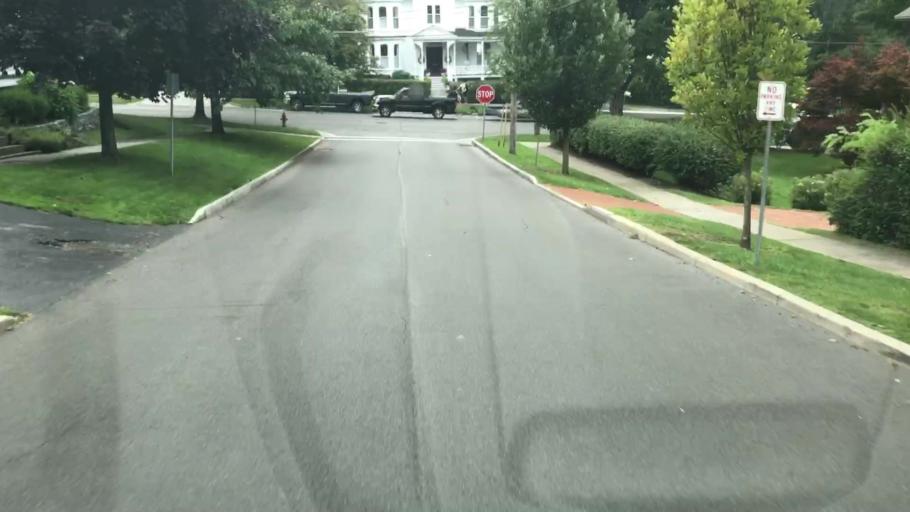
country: US
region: New York
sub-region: Onondaga County
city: Skaneateles
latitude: 42.9458
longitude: -76.4238
